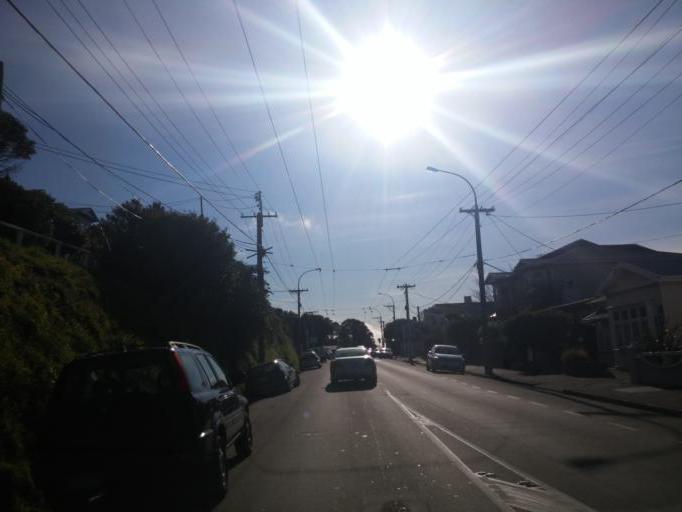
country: NZ
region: Wellington
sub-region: Wellington City
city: Brooklyn
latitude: -41.3051
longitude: 174.7633
